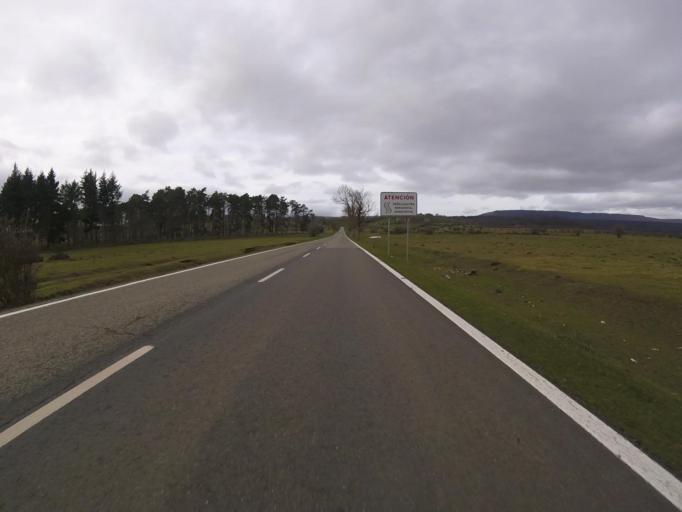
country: ES
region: Navarre
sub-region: Provincia de Navarra
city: Eulate
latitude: 42.8113
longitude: -2.1603
